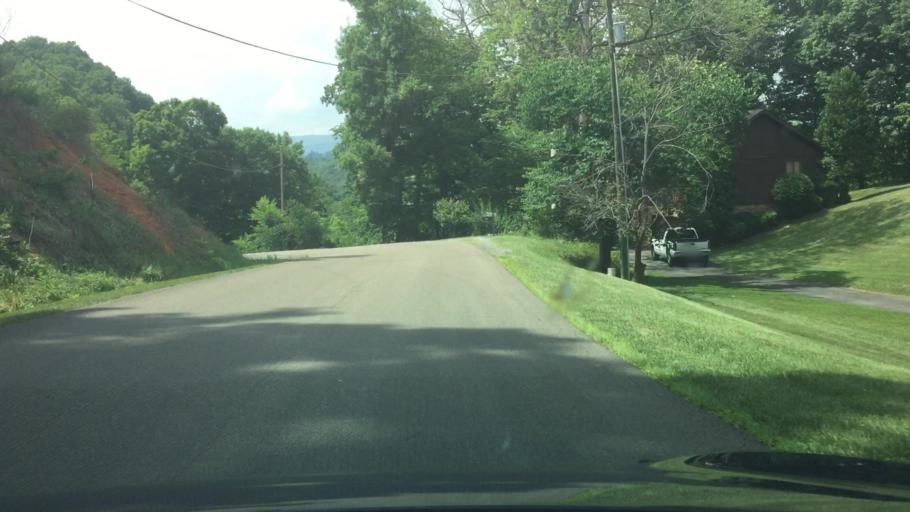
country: US
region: Virginia
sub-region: Wythe County
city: Wytheville
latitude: 36.9288
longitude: -81.0663
